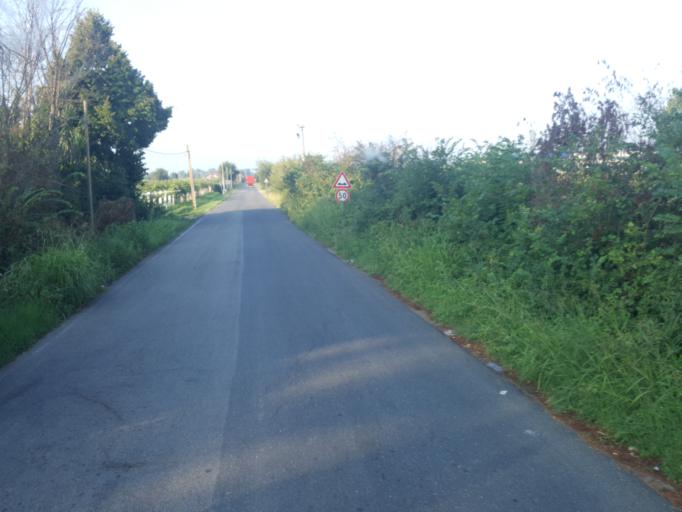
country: IT
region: Latium
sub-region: Provincia di Latina
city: Cisterna di Latina
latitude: 41.5649
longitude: 12.8711
